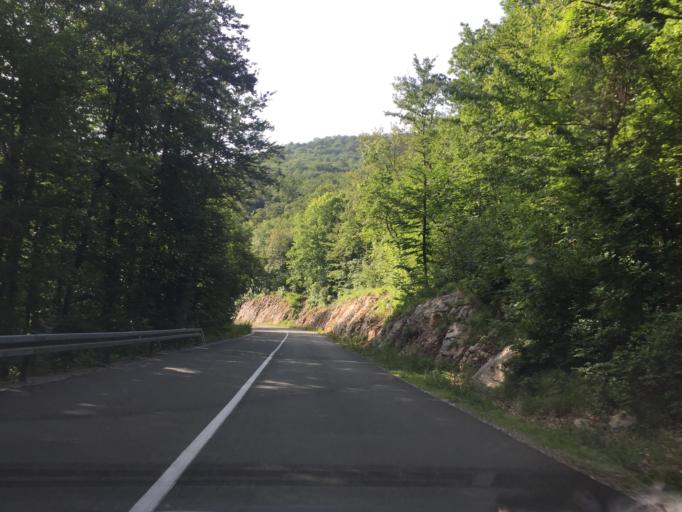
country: HR
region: Primorsko-Goranska
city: Matulji
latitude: 45.4072
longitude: 14.2548
